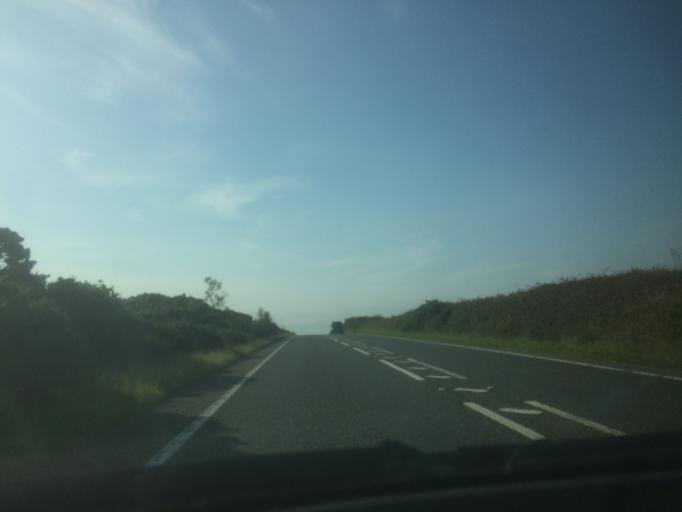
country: GB
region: England
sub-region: Cornwall
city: Callington
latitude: 50.4842
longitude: -4.2866
